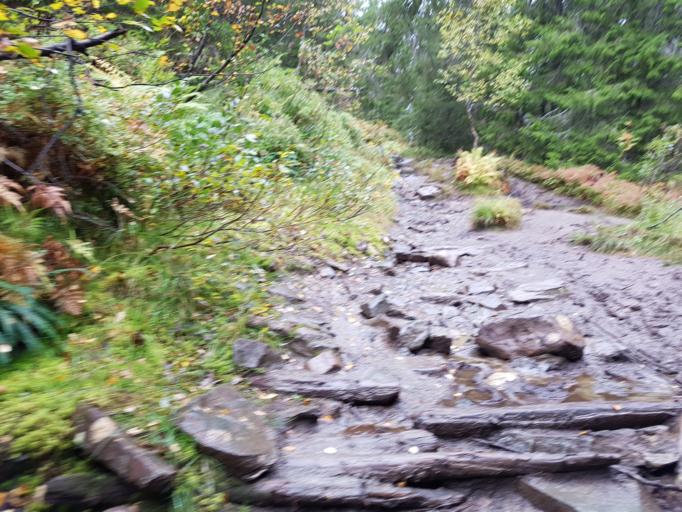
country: NO
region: Sor-Trondelag
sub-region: Melhus
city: Melhus
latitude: 63.4151
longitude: 10.2252
